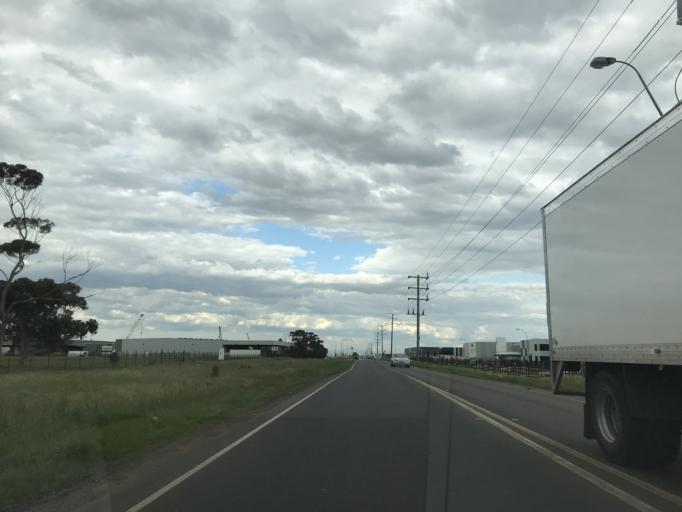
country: AU
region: Victoria
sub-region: Wyndham
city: Truganina
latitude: -37.8242
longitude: 144.7401
